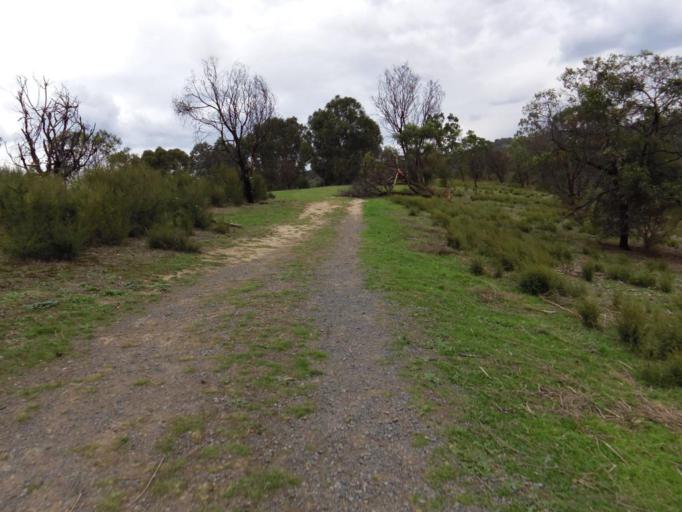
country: AU
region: Victoria
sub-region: Yarra Ranges
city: Chirnside Park
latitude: -37.7173
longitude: 145.2899
